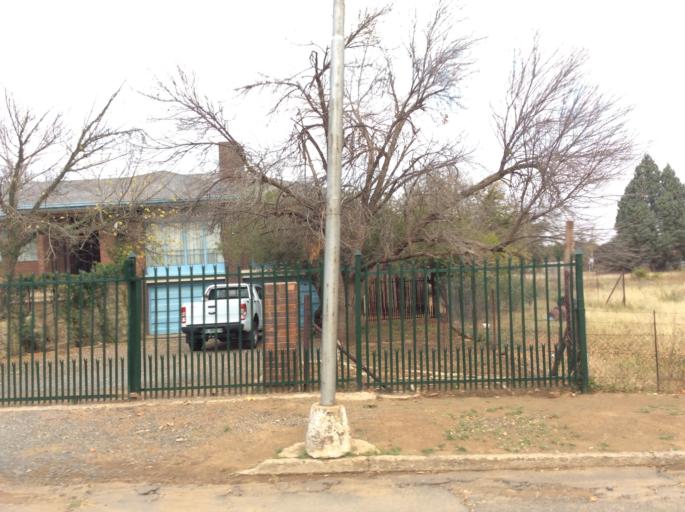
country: LS
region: Mafeteng
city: Mafeteng
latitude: -29.7275
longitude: 27.0416
